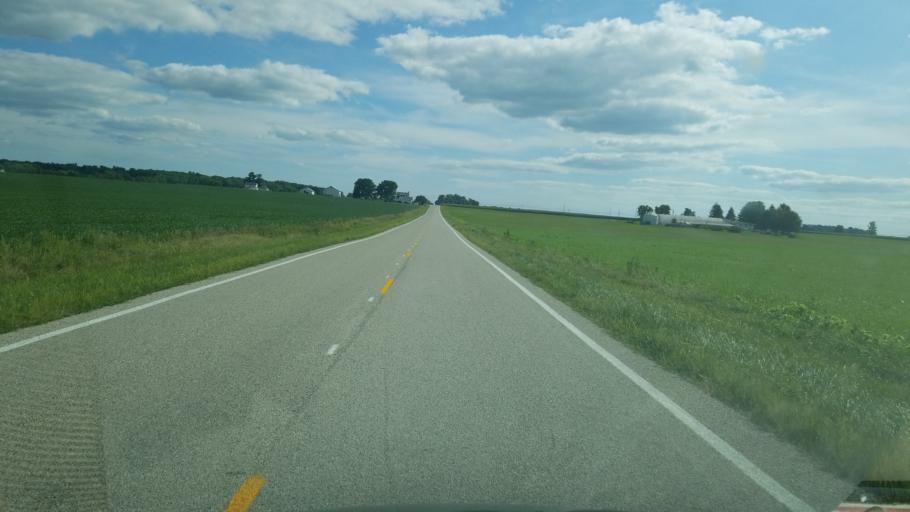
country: US
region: Ohio
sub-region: Logan County
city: De Graff
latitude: 40.2232
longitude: -83.9406
